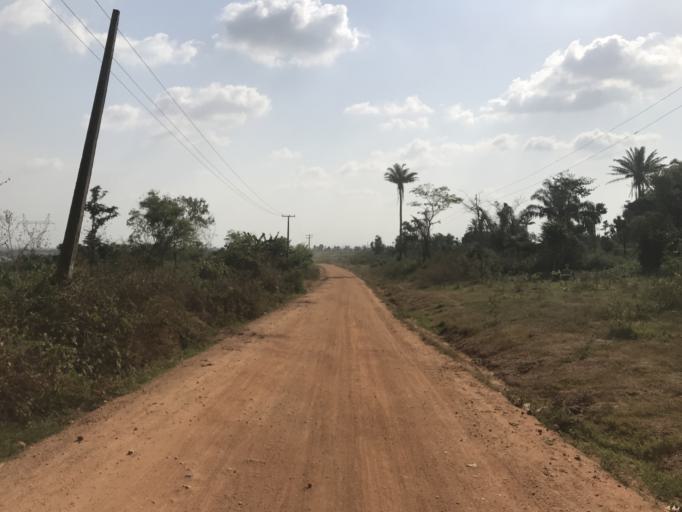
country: NG
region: Osun
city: Osogbo
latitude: 7.8378
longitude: 4.5719
